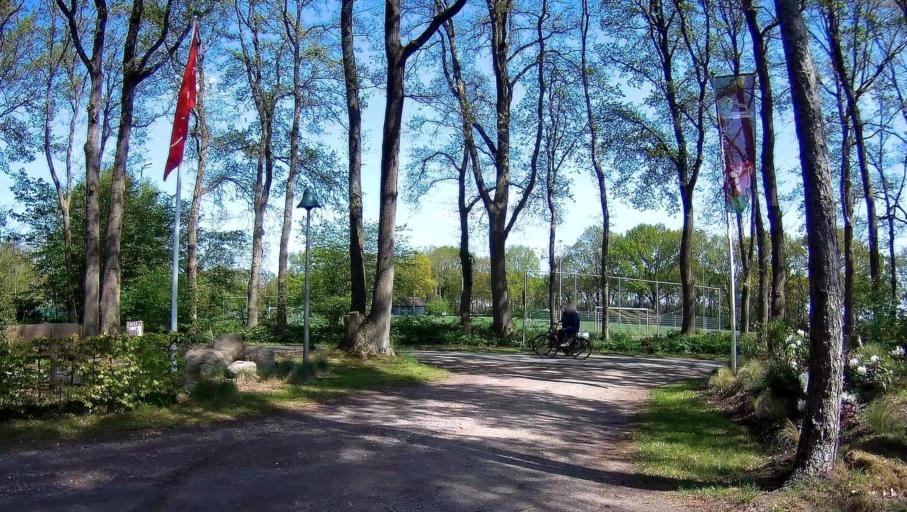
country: NL
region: Drenthe
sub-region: Gemeente Borger-Odoorn
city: Borger
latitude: 52.9710
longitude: 6.8074
